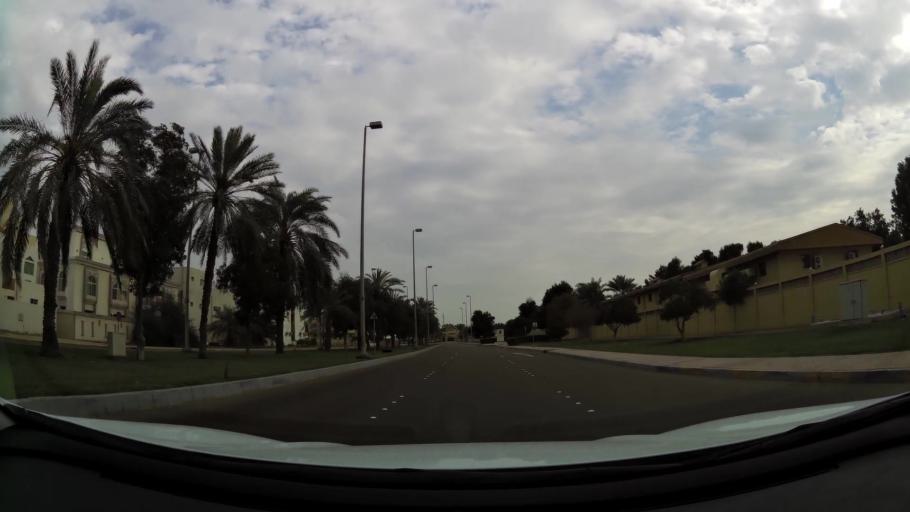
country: AE
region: Abu Dhabi
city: Abu Dhabi
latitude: 24.4424
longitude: 54.3880
